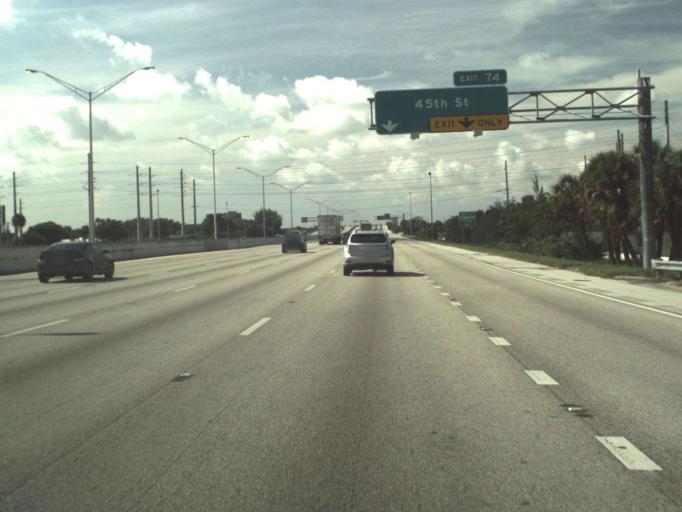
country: US
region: Florida
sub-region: Palm Beach County
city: Mangonia Park
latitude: 26.7676
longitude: -80.0948
